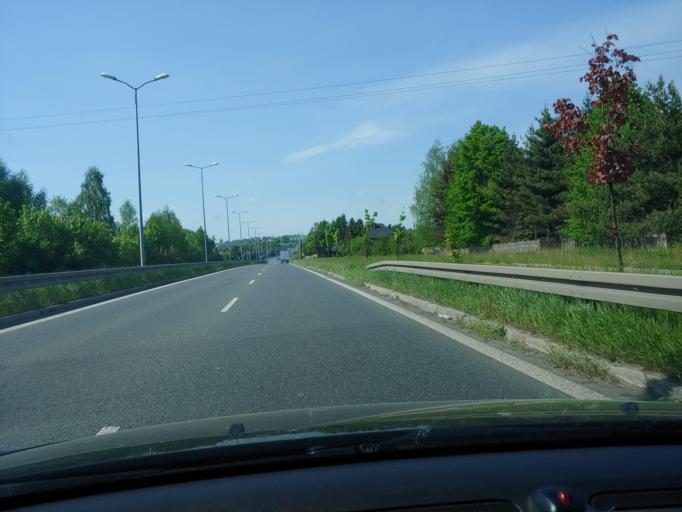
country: PL
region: Silesian Voivodeship
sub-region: Jaworzno
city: Jaworzno
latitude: 50.1774
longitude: 19.2932
